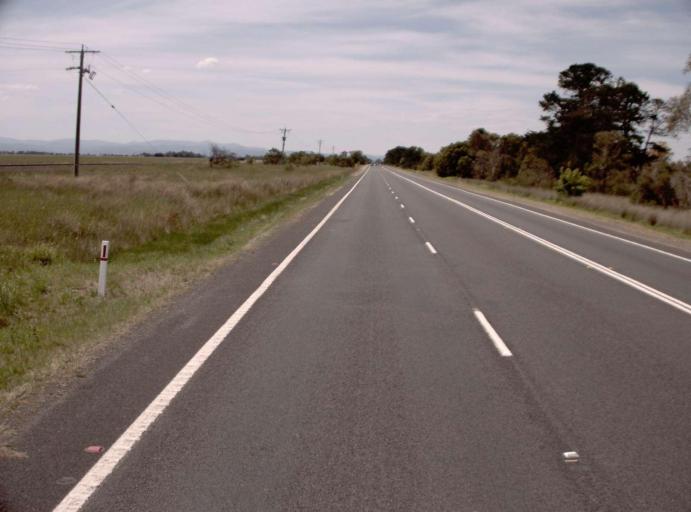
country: AU
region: Victoria
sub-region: Wellington
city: Sale
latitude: -38.0250
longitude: 147.0592
